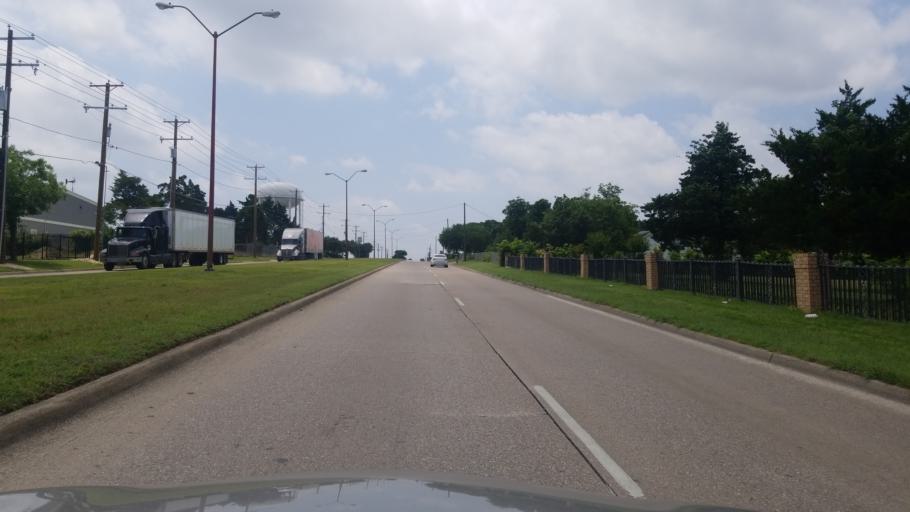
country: US
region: Texas
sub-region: Dallas County
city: Duncanville
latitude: 32.6789
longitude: -96.9087
